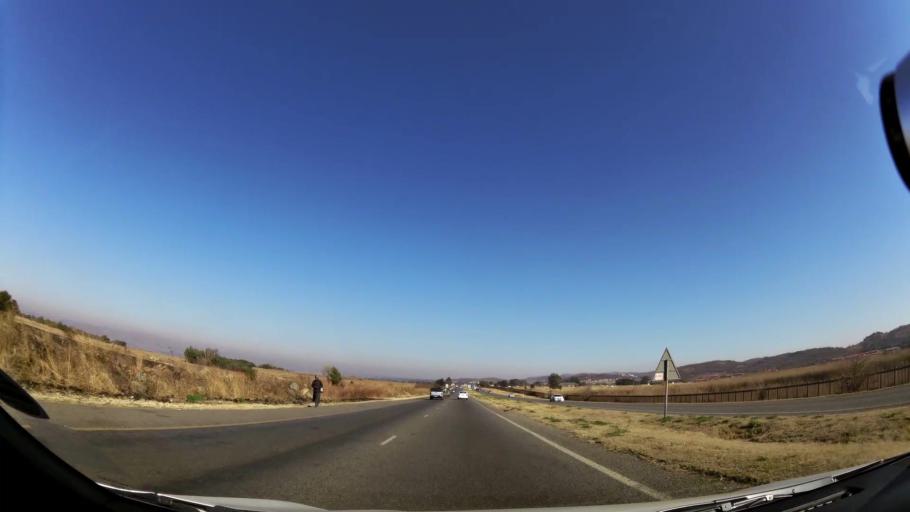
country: ZA
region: Gauteng
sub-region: Ekurhuleni Metropolitan Municipality
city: Germiston
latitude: -26.3121
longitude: 28.0887
